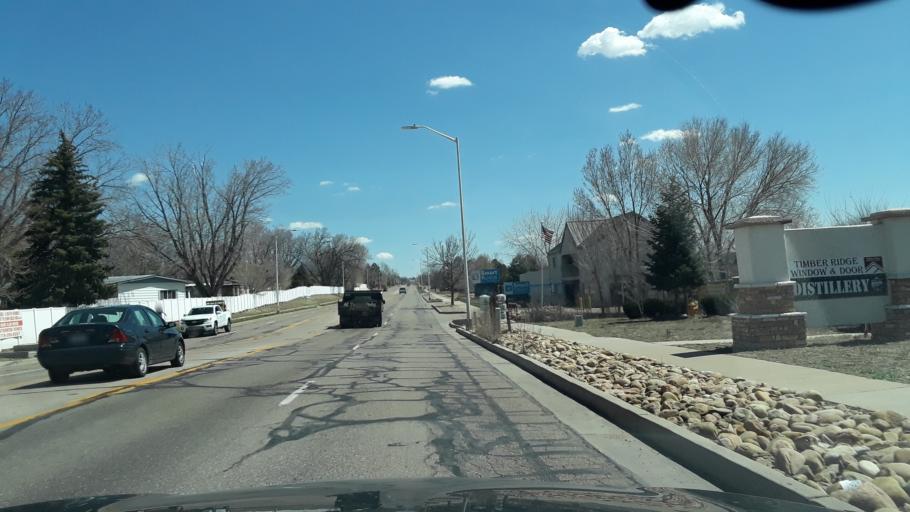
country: US
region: Colorado
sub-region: El Paso County
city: Cimarron Hills
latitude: 38.8470
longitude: -104.7373
